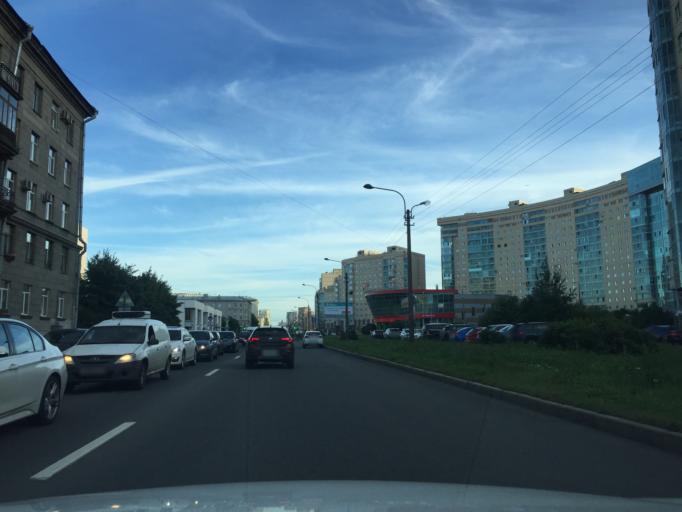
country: RU
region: St.-Petersburg
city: Kupchino
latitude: 59.8705
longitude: 30.3136
